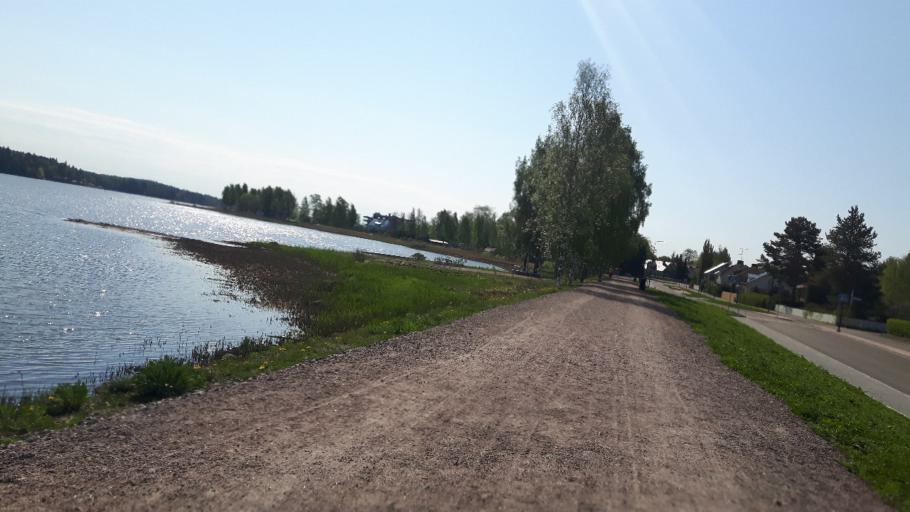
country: FI
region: Uusimaa
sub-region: Loviisa
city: Lovisa
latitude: 60.4503
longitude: 26.2345
